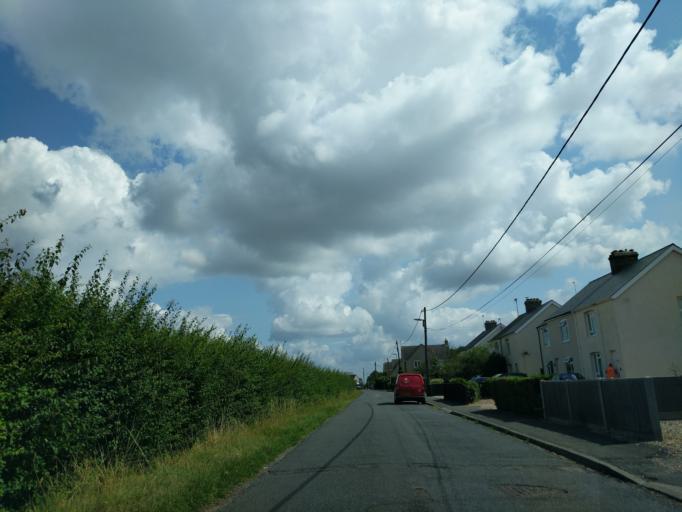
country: GB
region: England
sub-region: Cambridgeshire
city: Soham
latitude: 52.3145
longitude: 0.3759
